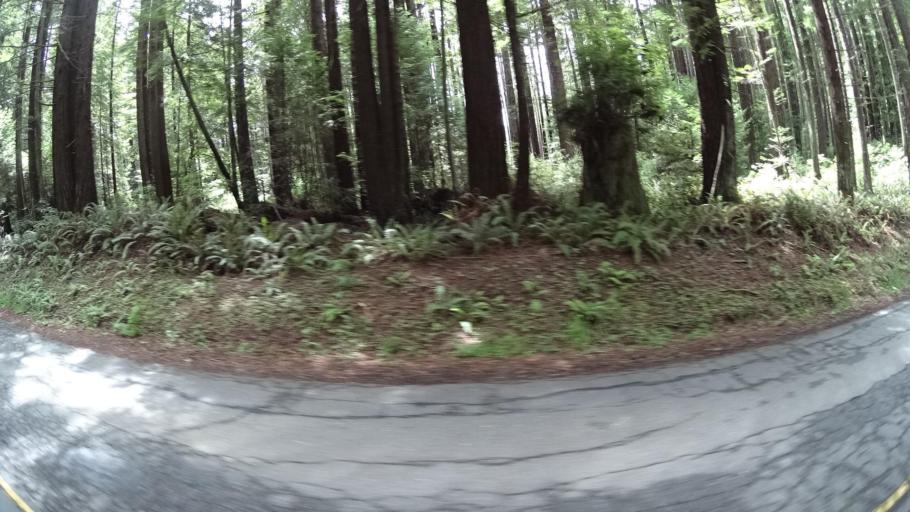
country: US
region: California
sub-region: Humboldt County
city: Myrtletown
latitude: 40.7878
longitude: -124.0796
